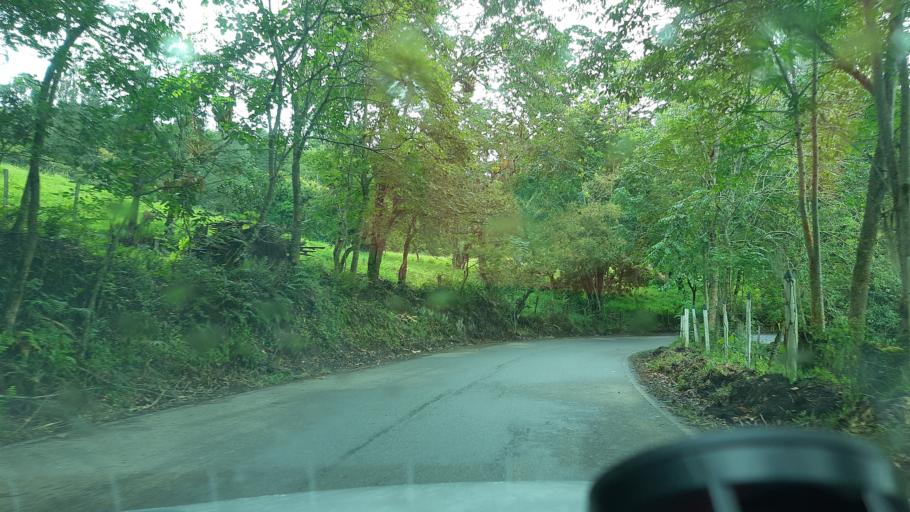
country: CO
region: Boyaca
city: Chinavita
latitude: 5.1540
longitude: -73.3647
